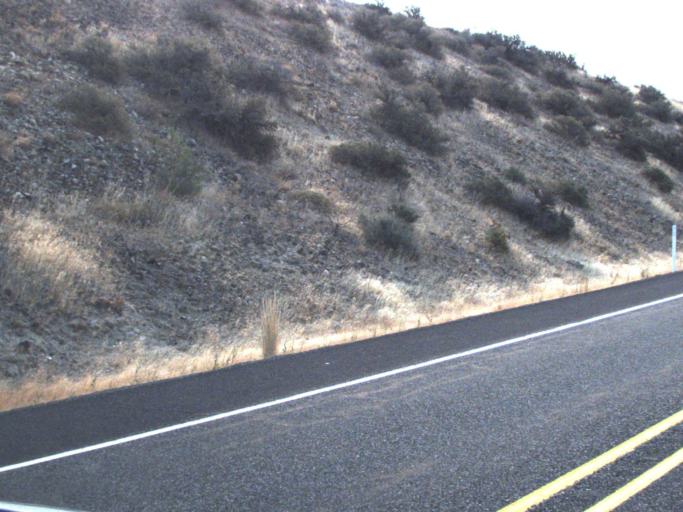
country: US
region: Washington
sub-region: Kittitas County
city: Ellensburg
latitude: 47.1464
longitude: -120.6935
